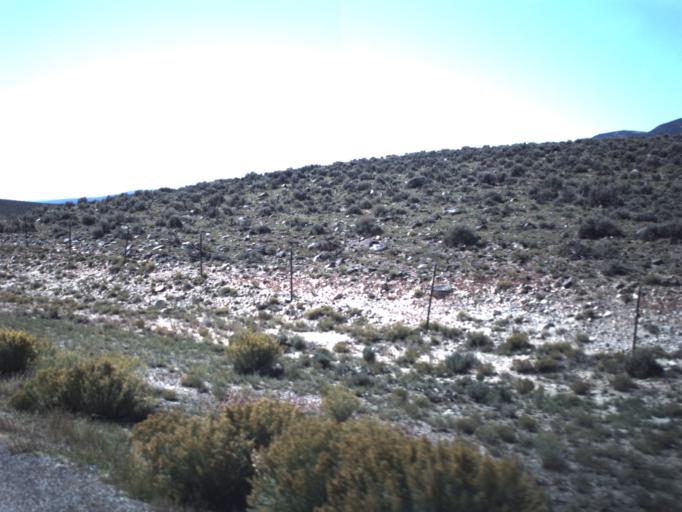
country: US
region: Utah
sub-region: Piute County
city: Junction
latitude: 38.2419
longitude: -111.9881
